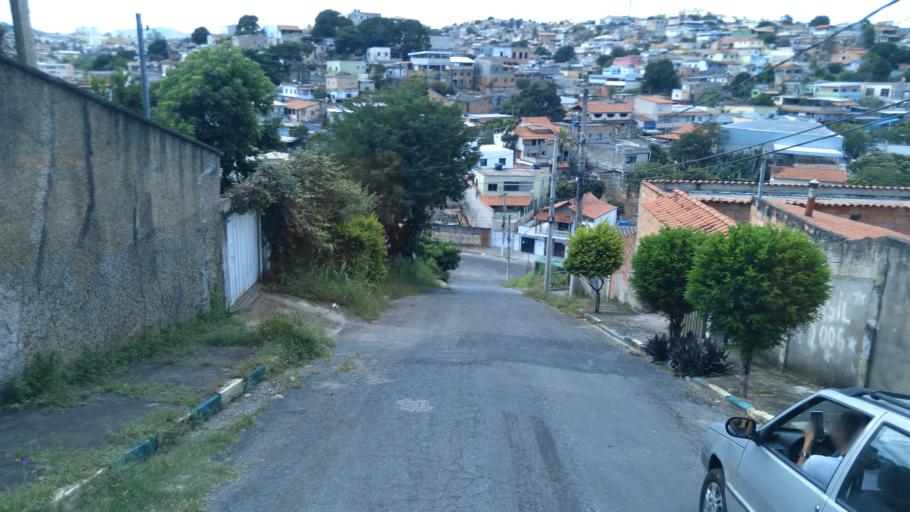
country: BR
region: Minas Gerais
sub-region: Belo Horizonte
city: Belo Horizonte
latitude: -19.8605
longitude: -43.9076
